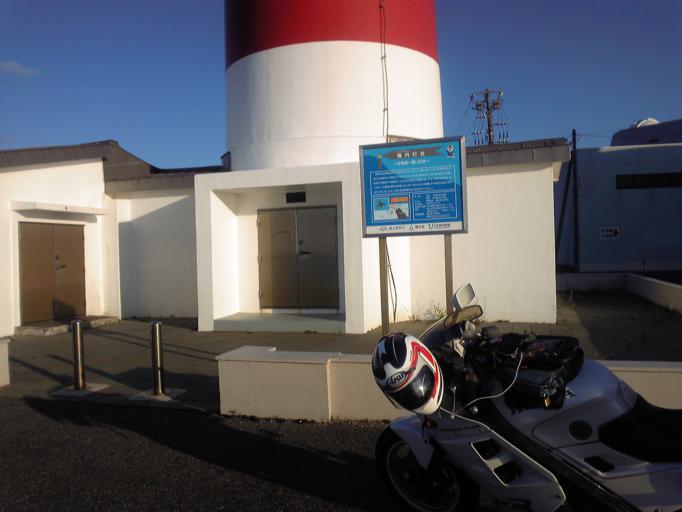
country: JP
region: Hokkaido
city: Wakkanai
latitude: 45.4495
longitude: 141.6450
